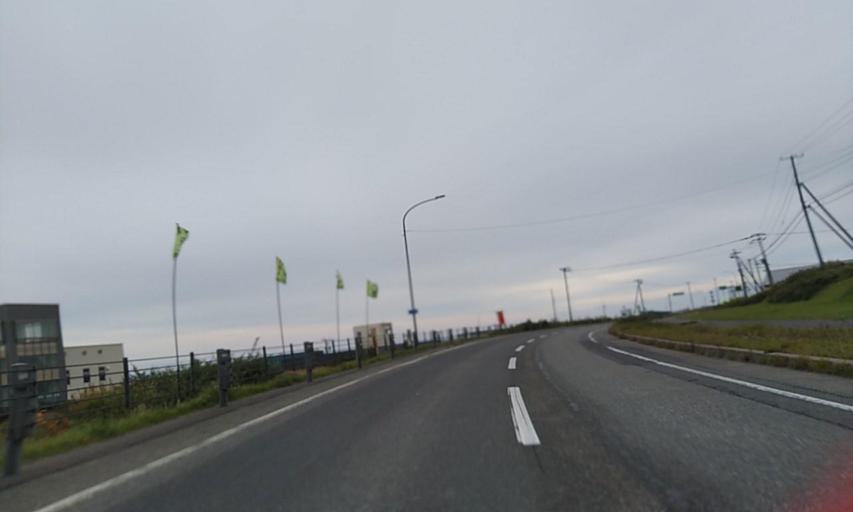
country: JP
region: Hokkaido
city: Makubetsu
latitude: 45.3404
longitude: 142.1655
